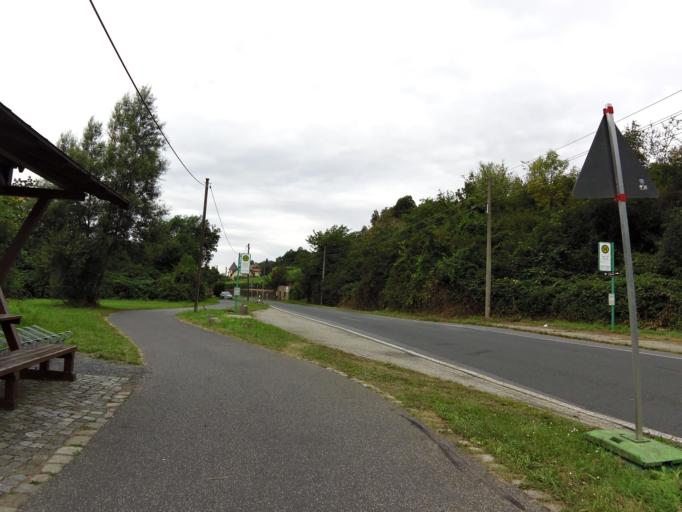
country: DE
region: Saxony
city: Meissen
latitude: 51.1820
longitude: 13.4571
